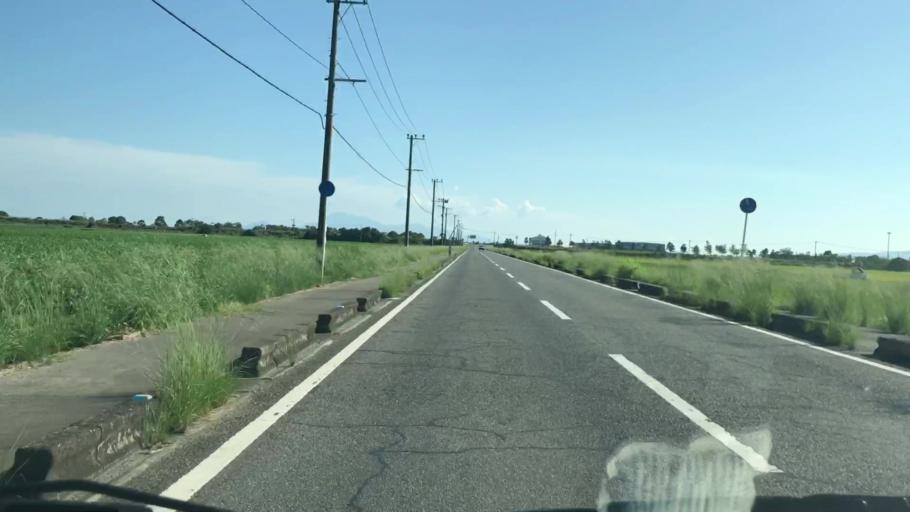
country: JP
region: Saga Prefecture
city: Okawa
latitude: 33.1580
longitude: 130.3084
